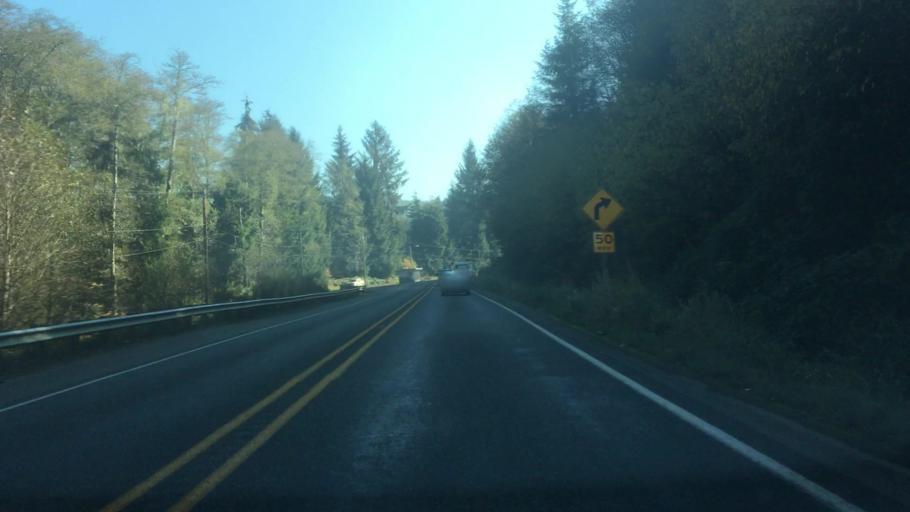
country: US
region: Washington
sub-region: Grays Harbor County
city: Central Park
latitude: 46.9160
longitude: -123.7179
